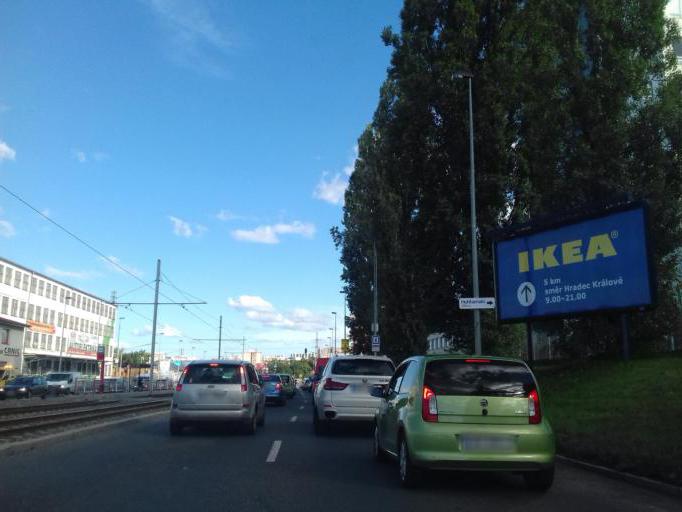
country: CZ
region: Praha
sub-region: Praha 9
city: Vysocany
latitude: 50.1036
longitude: 14.5236
